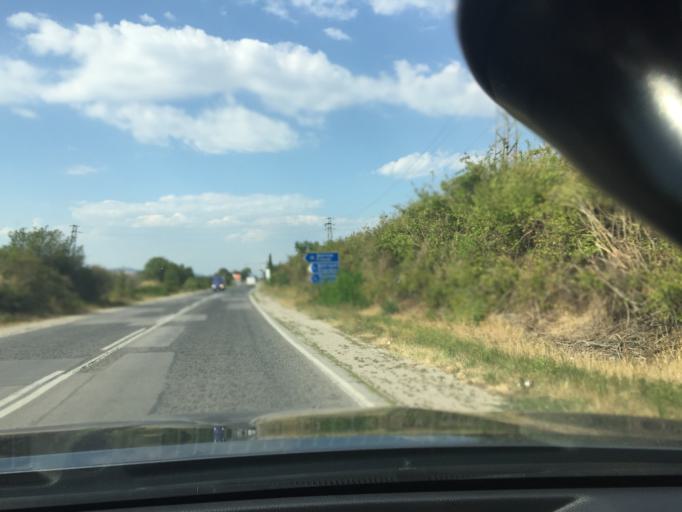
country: BG
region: Kyustendil
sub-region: Obshtina Kocherinovo
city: Kocherinovo
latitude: 42.1117
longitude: 23.0379
